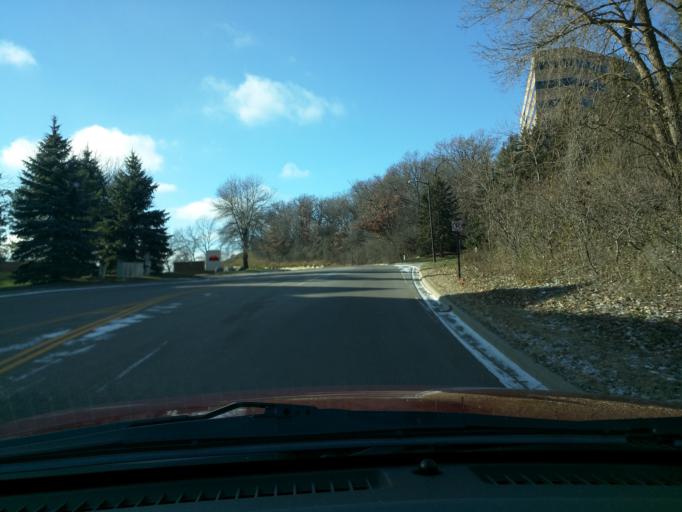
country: US
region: Minnesota
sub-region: Hennepin County
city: Eden Prairie
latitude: 44.8666
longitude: -93.4141
